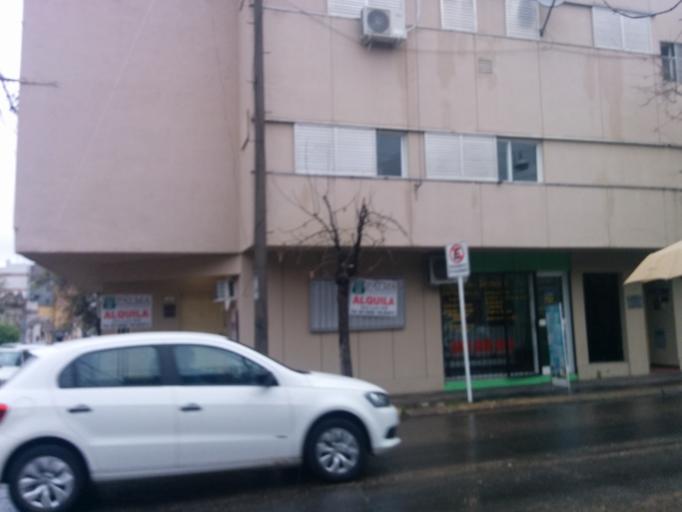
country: AR
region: Entre Rios
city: Concordia
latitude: -31.3946
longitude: -58.0151
